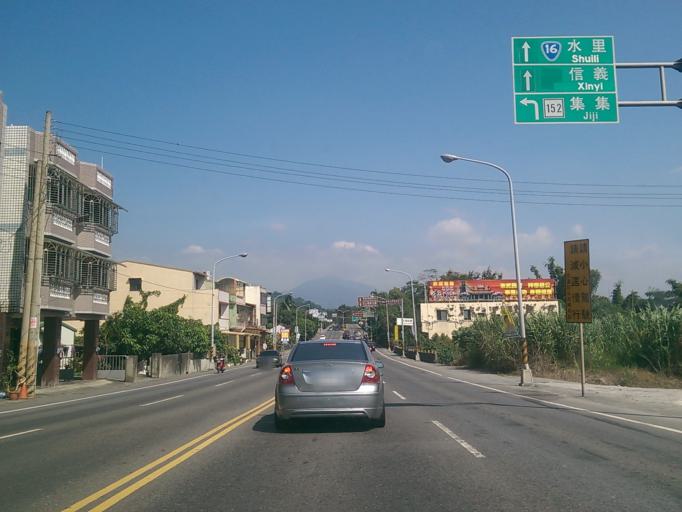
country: TW
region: Taiwan
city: Lugu
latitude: 23.8347
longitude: 120.7203
